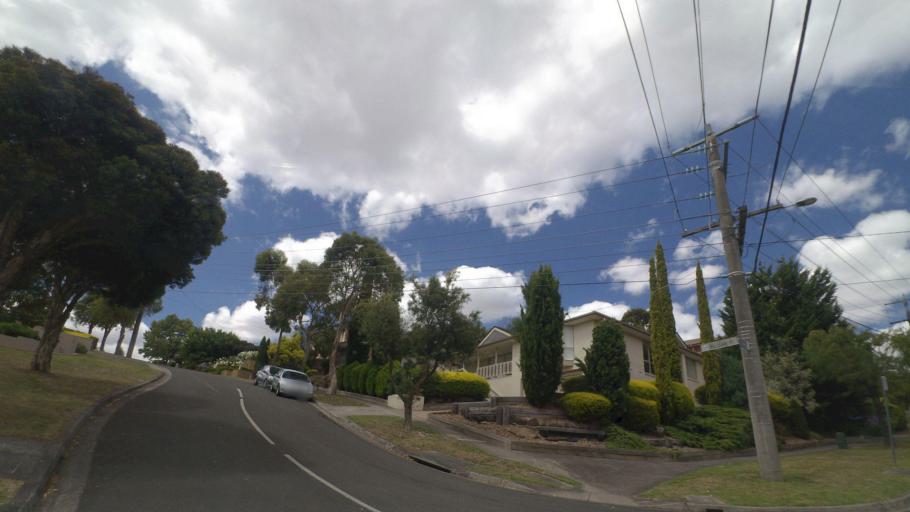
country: AU
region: Victoria
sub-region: Maroondah
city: Warranwood
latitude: -37.7757
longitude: 145.2433
